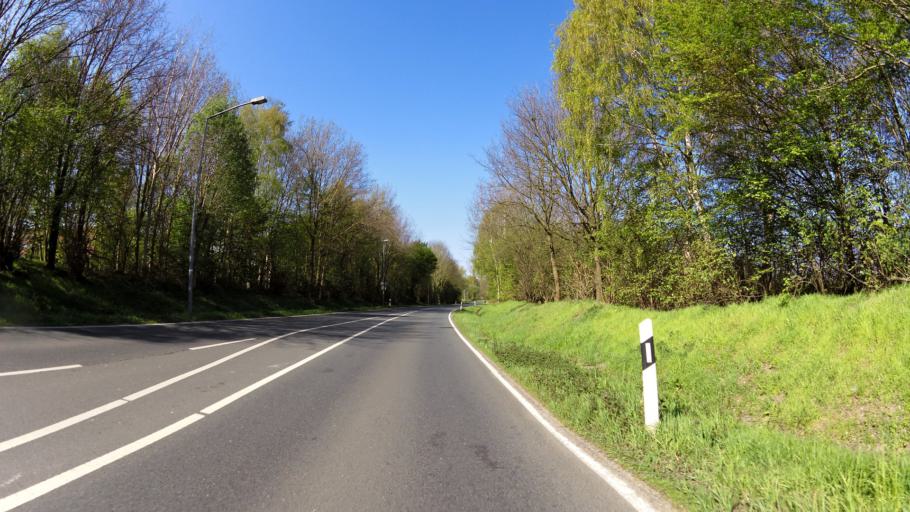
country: DE
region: Lower Saxony
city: Syke
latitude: 52.9254
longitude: 8.8155
